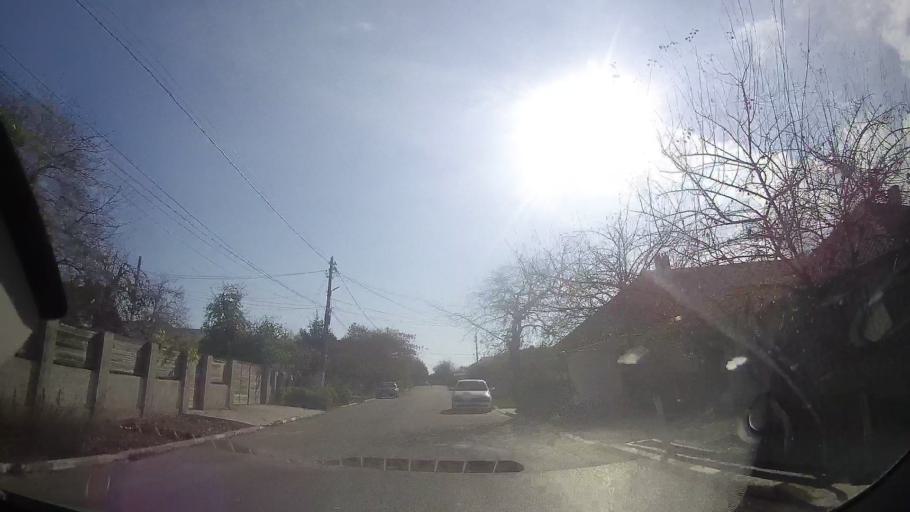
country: RO
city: Eforie Sud
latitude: 44.0109
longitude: 28.6444
